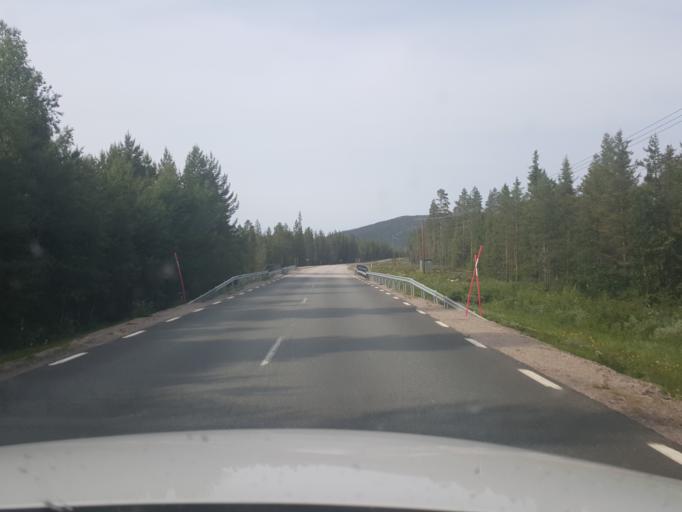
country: SE
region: Norrbotten
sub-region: Arjeplogs Kommun
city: Arjeplog
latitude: 65.8525
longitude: 18.0420
